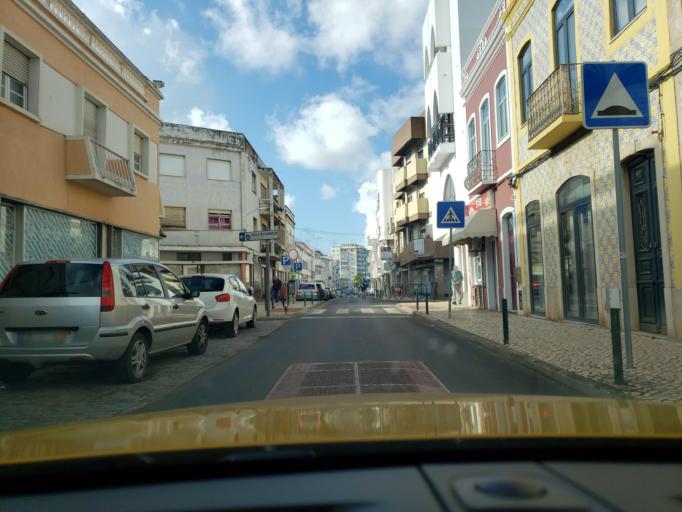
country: PT
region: Faro
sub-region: Portimao
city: Portimao
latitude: 37.1425
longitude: -8.5372
